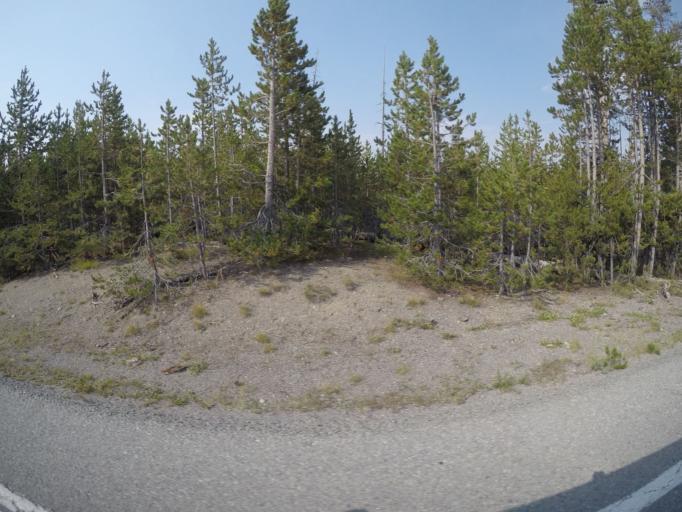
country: US
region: Montana
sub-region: Gallatin County
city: West Yellowstone
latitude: 44.7188
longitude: -110.6547
